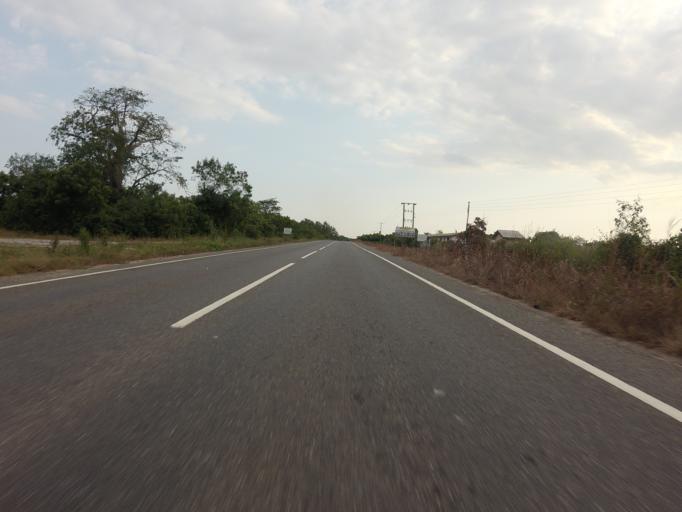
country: GH
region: Volta
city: Ho
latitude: 6.1139
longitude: 0.5179
